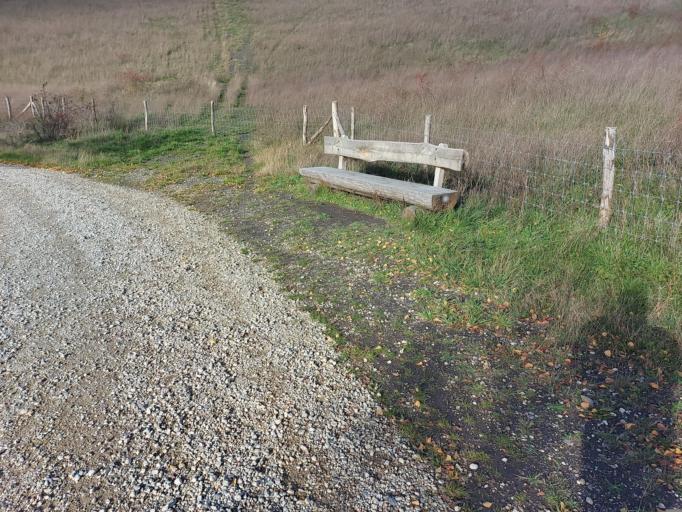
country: BE
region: Flanders
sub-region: Provincie Limburg
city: As
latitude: 51.0060
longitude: 5.5454
